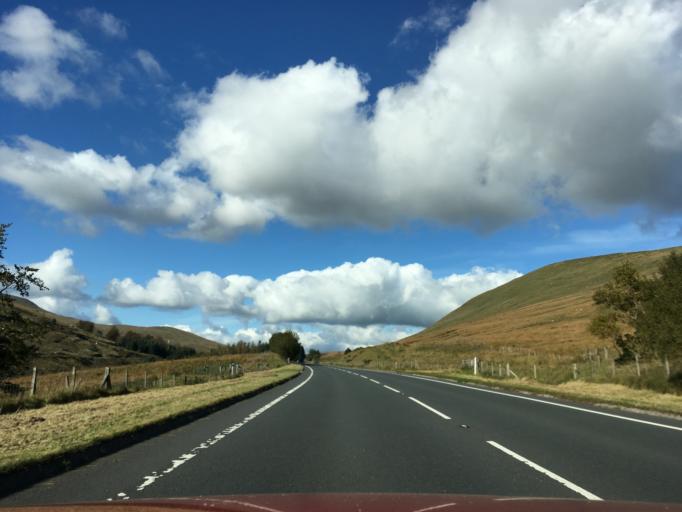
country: GB
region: Wales
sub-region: Rhondda Cynon Taf
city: Hirwaun
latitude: 51.8444
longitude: -3.4644
